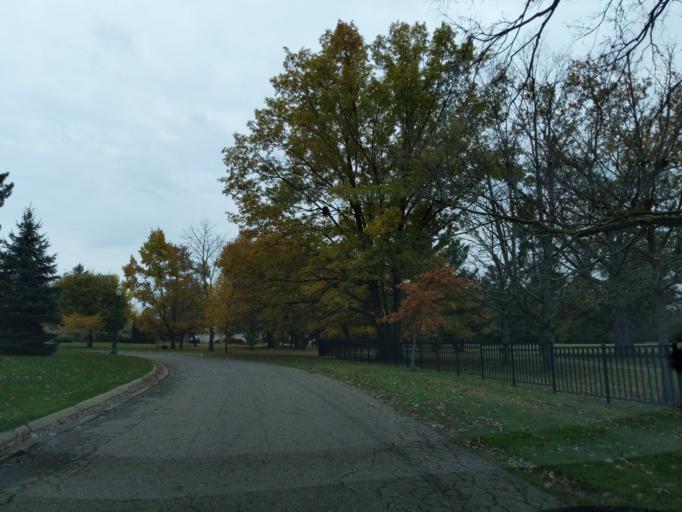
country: US
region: Michigan
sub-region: Ingham County
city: Edgemont Park
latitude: 42.7172
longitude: -84.5870
